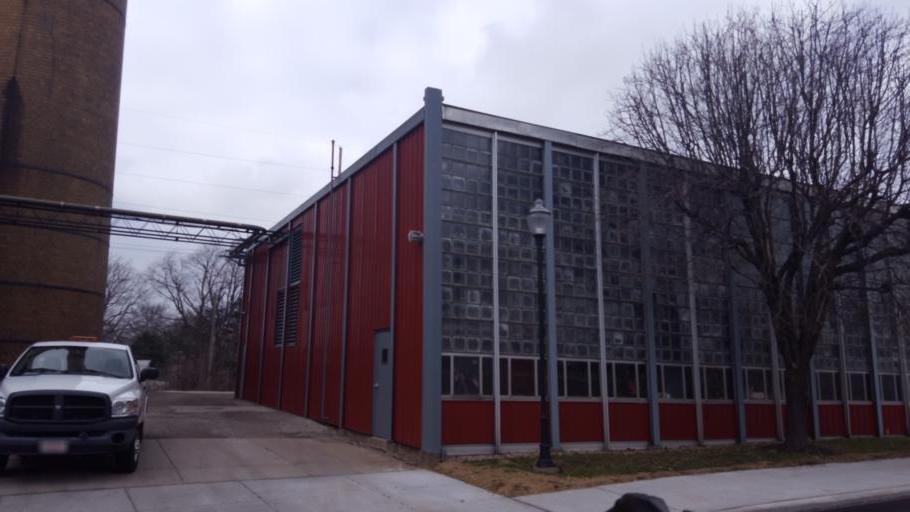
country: US
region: Ohio
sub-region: Richland County
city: Shelby
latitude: 40.8798
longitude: -82.6564
